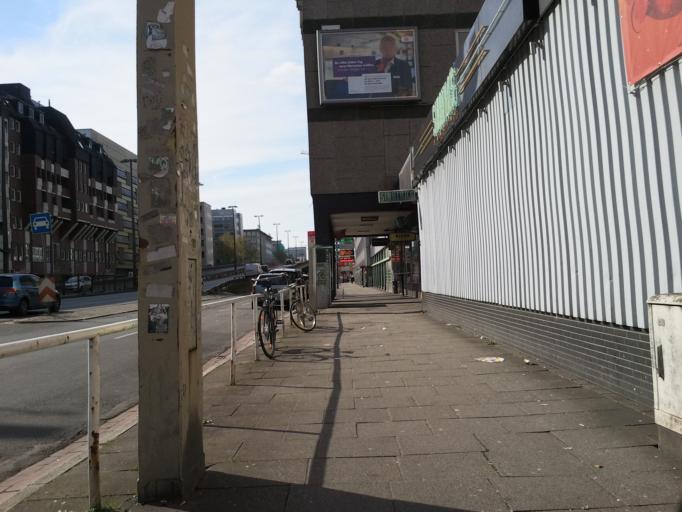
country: DE
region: Bremen
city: Bremen
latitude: 53.0794
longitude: 8.8158
